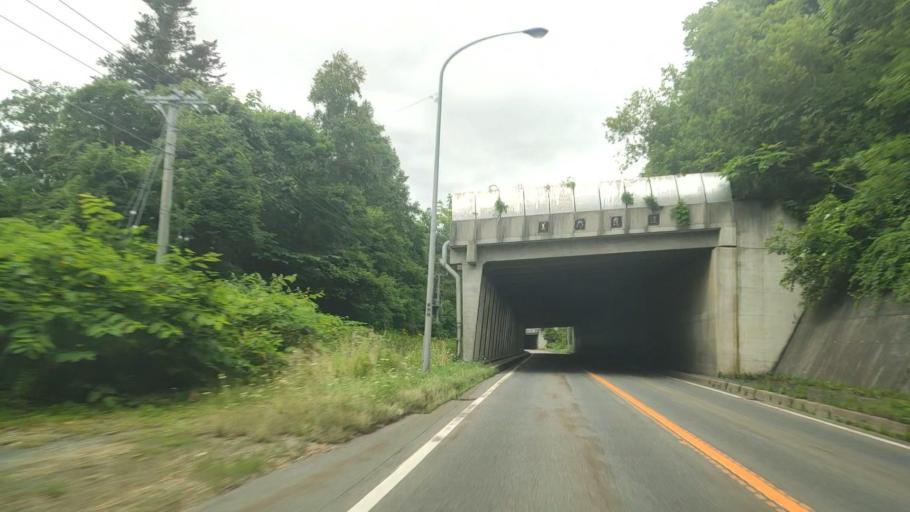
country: JP
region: Hokkaido
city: Niseko Town
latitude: 42.6011
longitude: 140.5719
